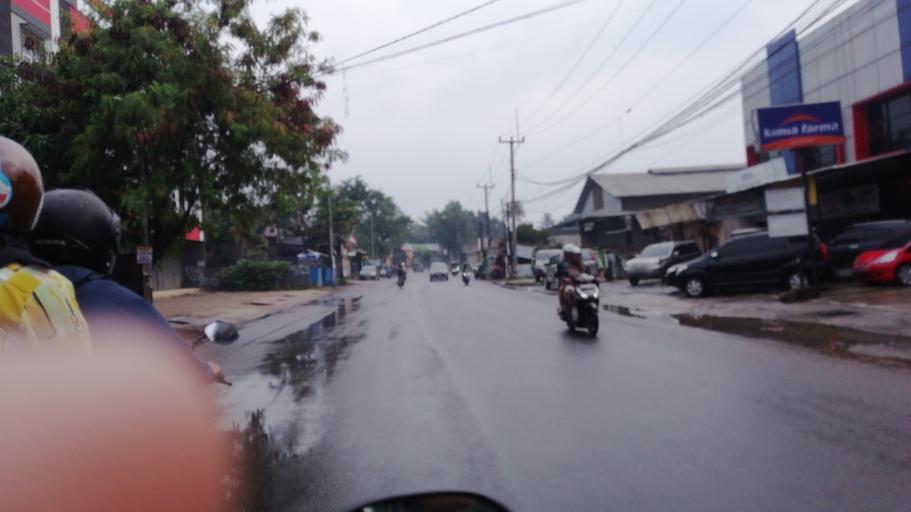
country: ID
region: West Java
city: Cibinong
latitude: -6.5295
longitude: 106.8102
